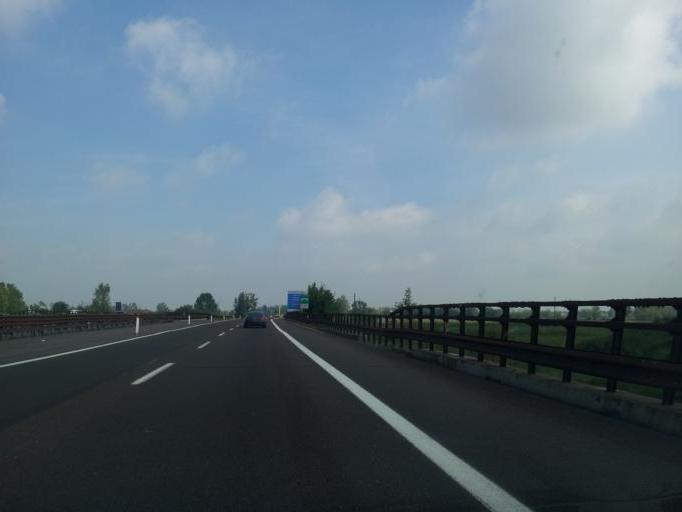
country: IT
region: Emilia-Romagna
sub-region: Provincia di Reggio Emilia
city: Rolo
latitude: 44.9026
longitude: 10.8488
